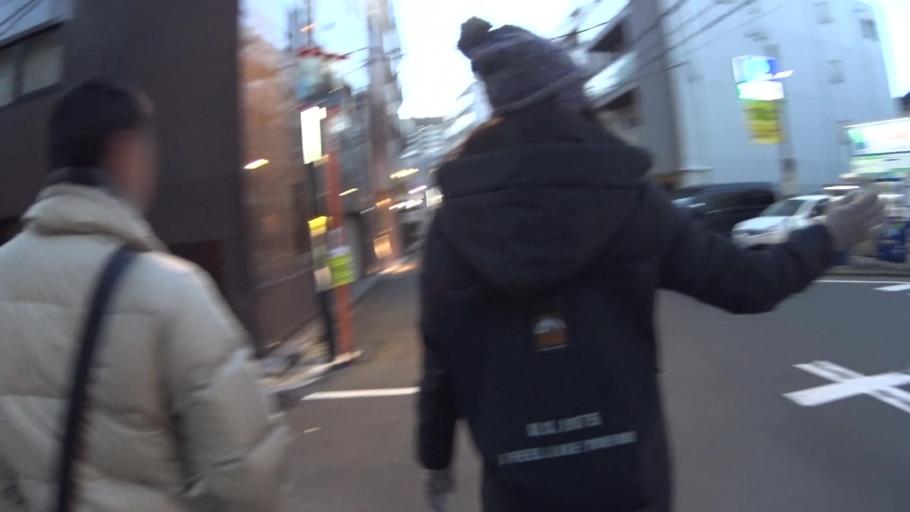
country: JP
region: Tokyo
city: Tokyo
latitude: 35.6789
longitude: 139.7084
